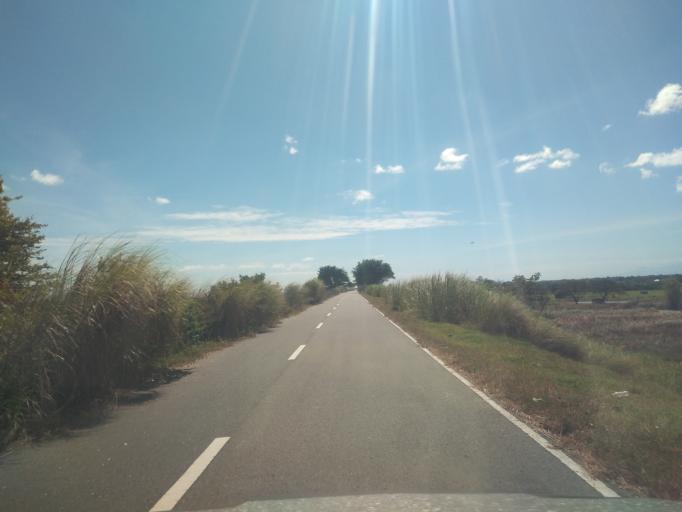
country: PH
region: Central Luzon
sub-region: Province of Pampanga
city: San Basilio
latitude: 15.0395
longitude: 120.5948
